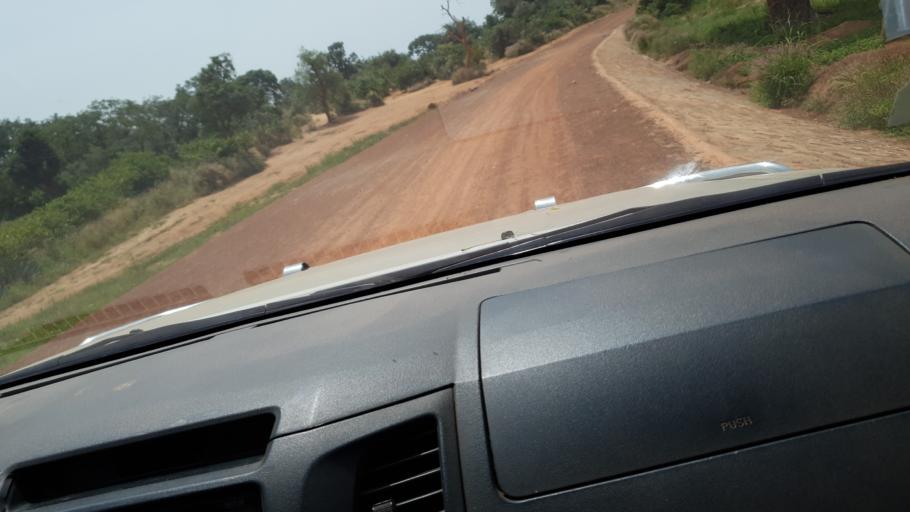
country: ML
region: Koulikoro
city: Kolokani
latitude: 13.4221
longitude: -8.2412
